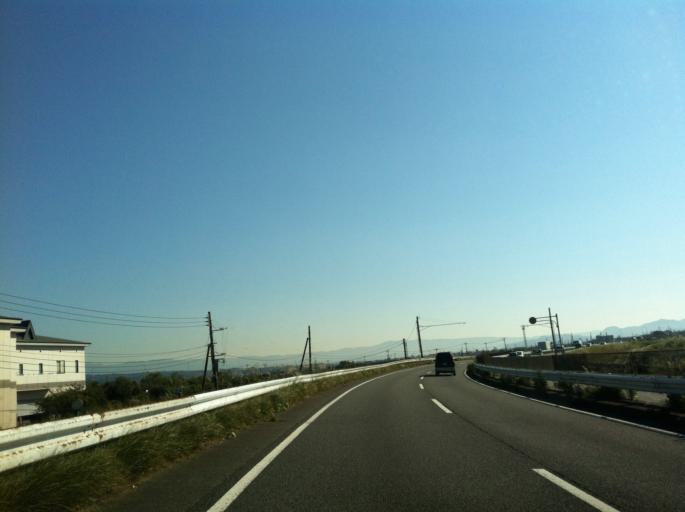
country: JP
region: Shizuoka
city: Numazu
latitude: 35.1345
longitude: 138.7836
